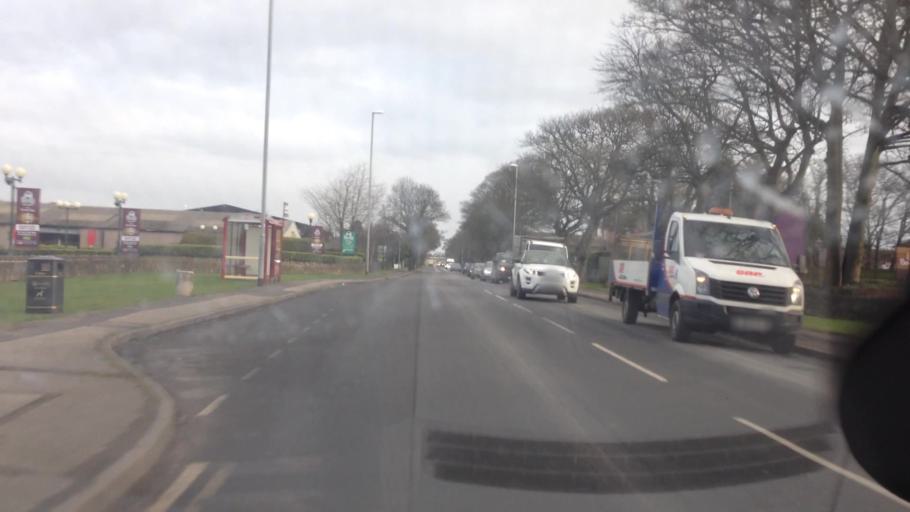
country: GB
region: England
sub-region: City and Borough of Leeds
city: Yeadon
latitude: 53.8635
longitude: -1.6725
